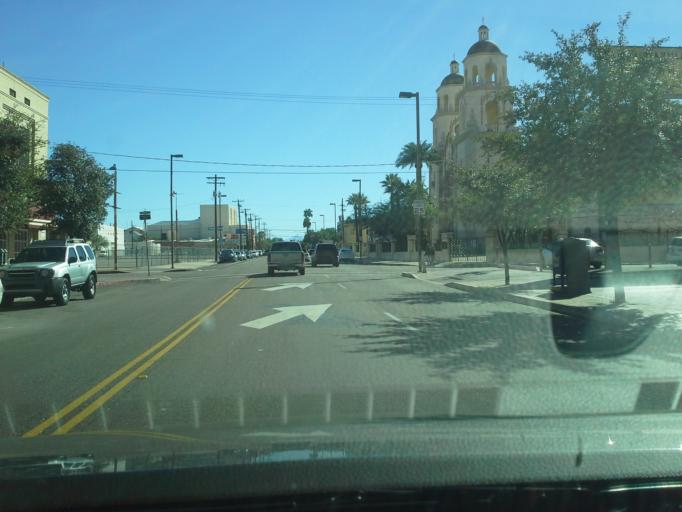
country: US
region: Arizona
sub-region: Pima County
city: South Tucson
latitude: 32.2203
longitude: -110.9710
